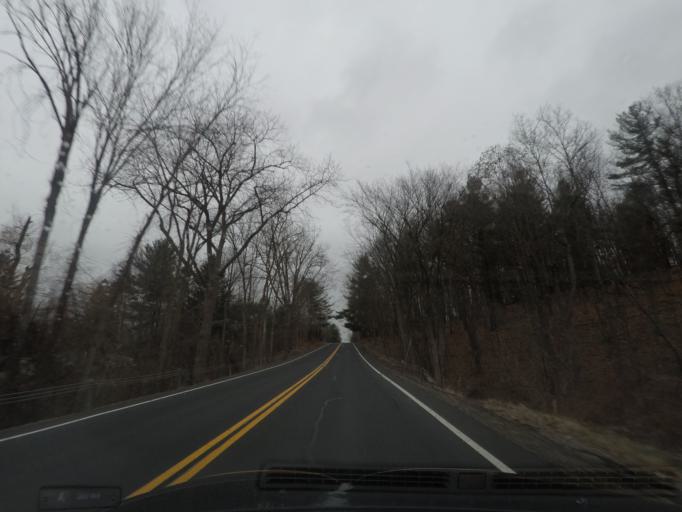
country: US
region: New York
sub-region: Rensselaer County
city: East Greenbush
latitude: 42.6058
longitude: -73.6555
